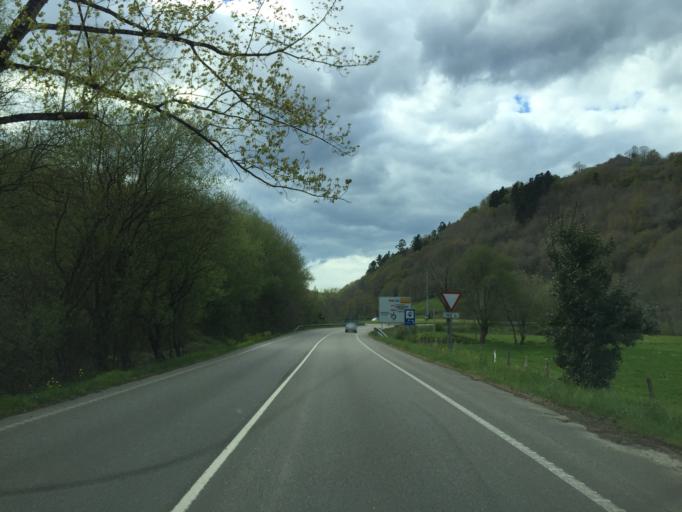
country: ES
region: Asturias
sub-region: Province of Asturias
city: Cangas de Onis
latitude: 43.3501
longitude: -5.1068
